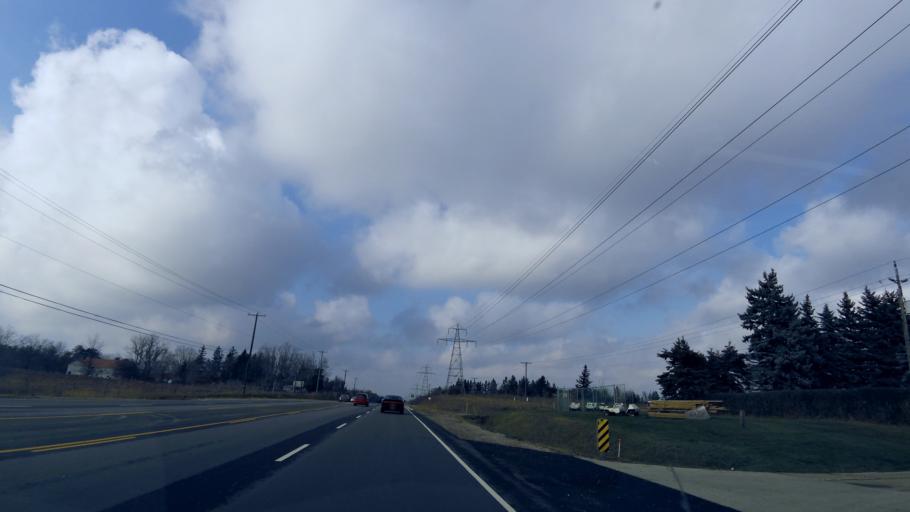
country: CA
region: Ontario
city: Ancaster
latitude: 43.3828
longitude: -80.0134
